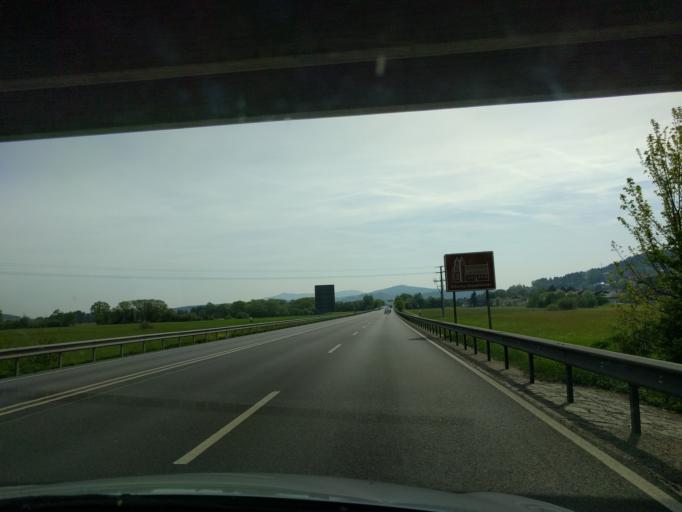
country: DE
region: Bavaria
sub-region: Upper Palatinate
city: Cham
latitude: 49.2137
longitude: 12.6850
